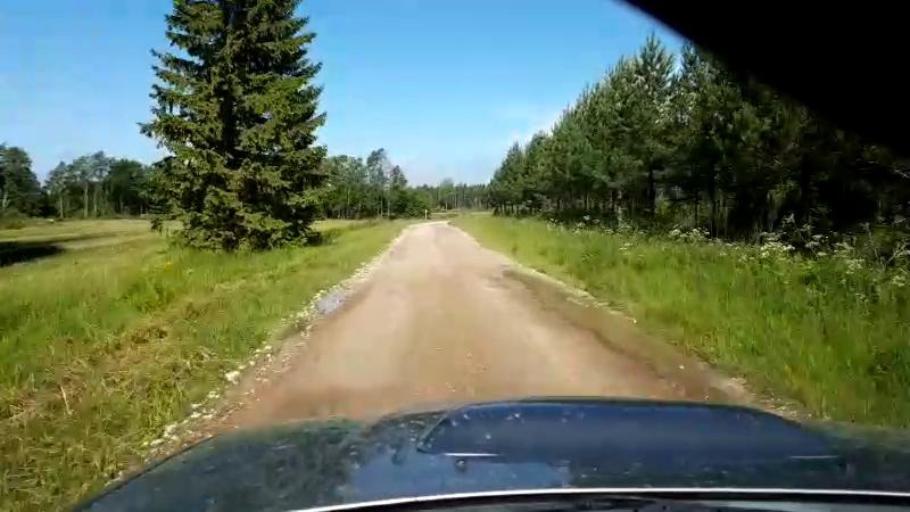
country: EE
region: Paernumaa
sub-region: Sindi linn
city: Sindi
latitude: 58.5102
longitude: 24.6881
